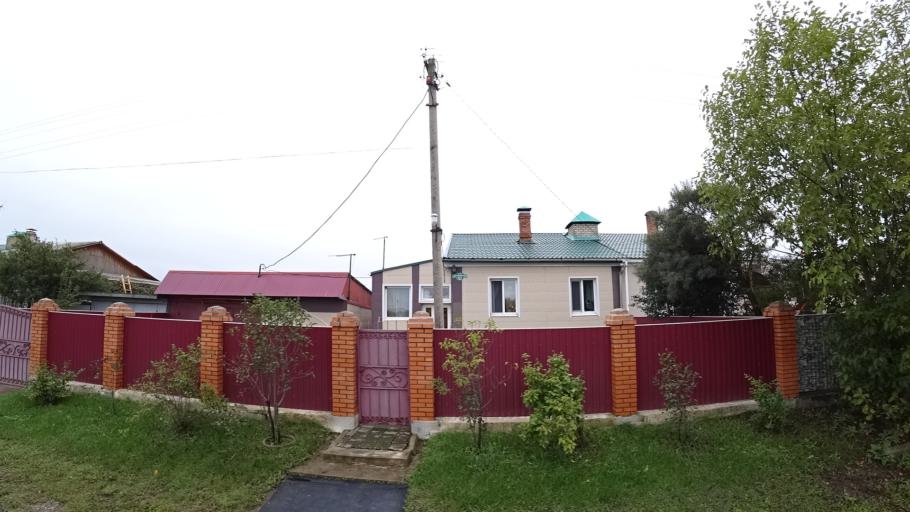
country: RU
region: Primorskiy
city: Monastyrishche
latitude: 44.2047
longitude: 132.4289
